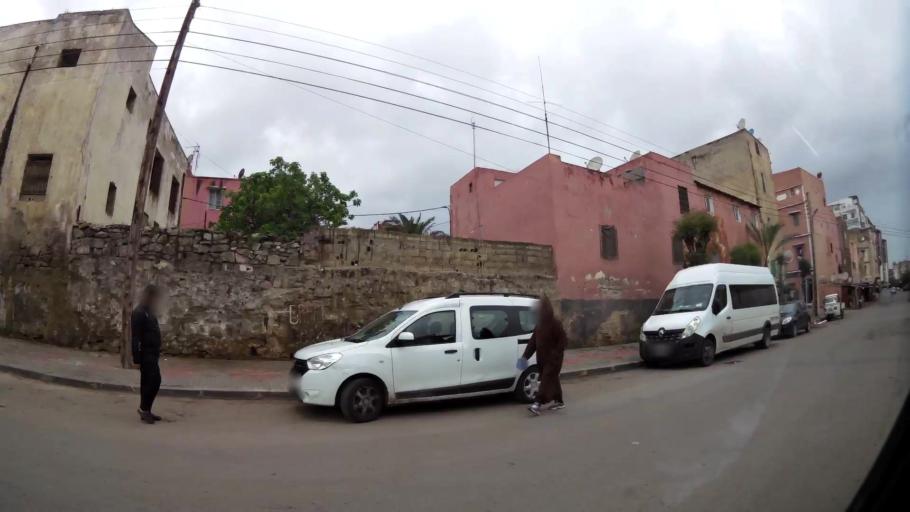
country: MA
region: Grand Casablanca
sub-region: Casablanca
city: Casablanca
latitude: 33.5685
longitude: -7.5939
